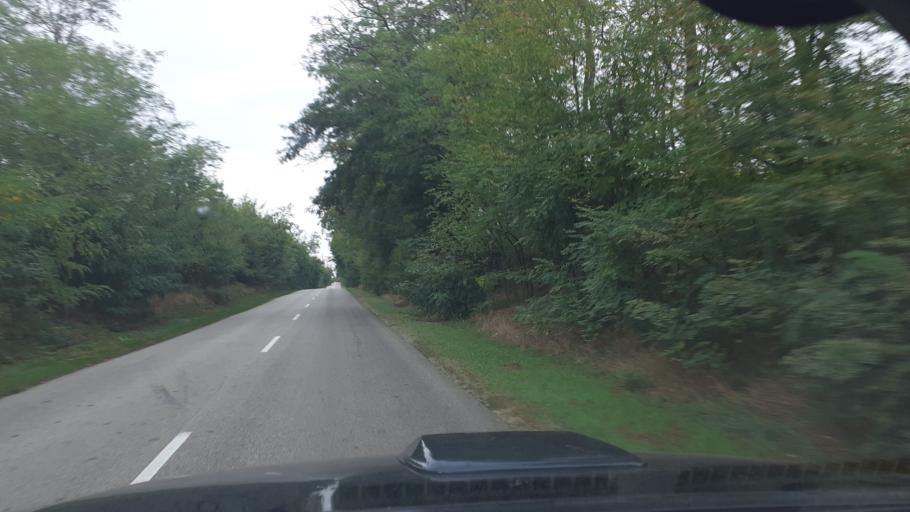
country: HU
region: Fejer
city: Baracs
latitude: 46.8487
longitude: 18.8851
